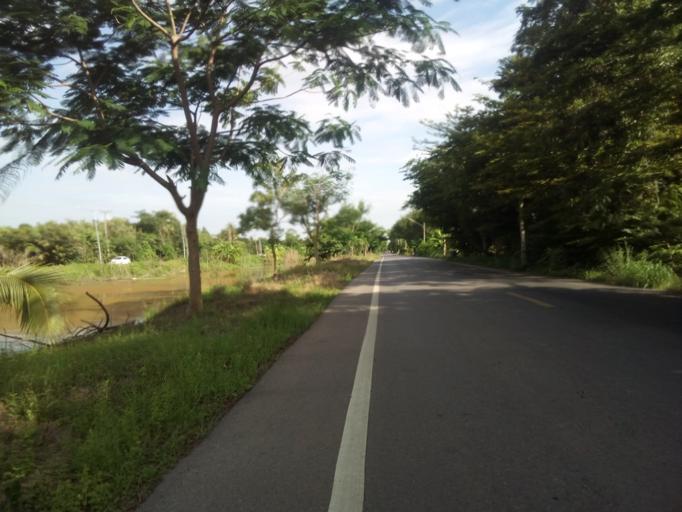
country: TH
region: Pathum Thani
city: Nong Suea
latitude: 14.1264
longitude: 100.8460
